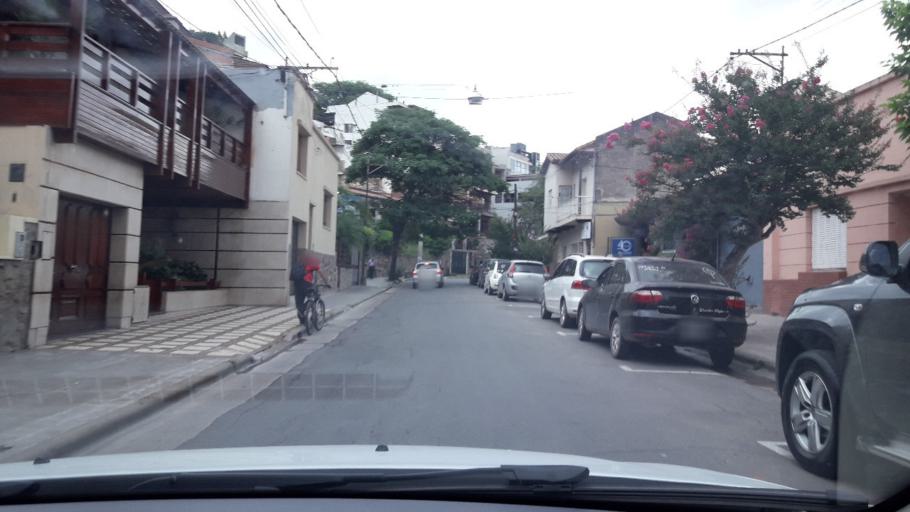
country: AR
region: Jujuy
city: San Salvador de Jujuy
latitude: -24.1858
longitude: -65.3118
